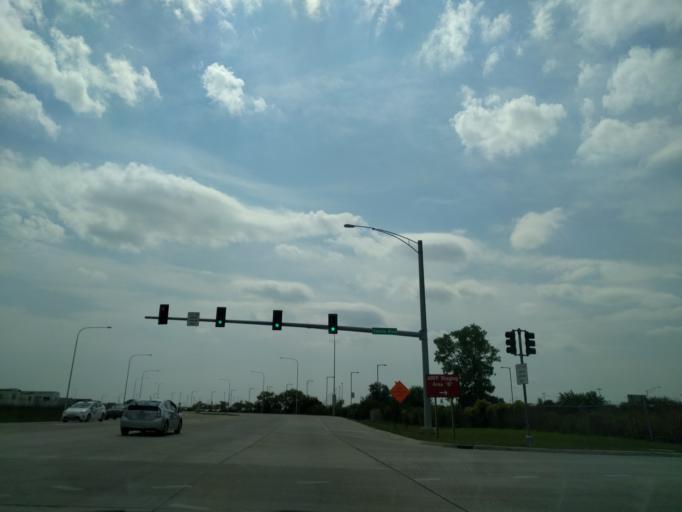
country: US
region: Illinois
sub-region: Cook County
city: Rosemont
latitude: 41.9950
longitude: -87.8847
